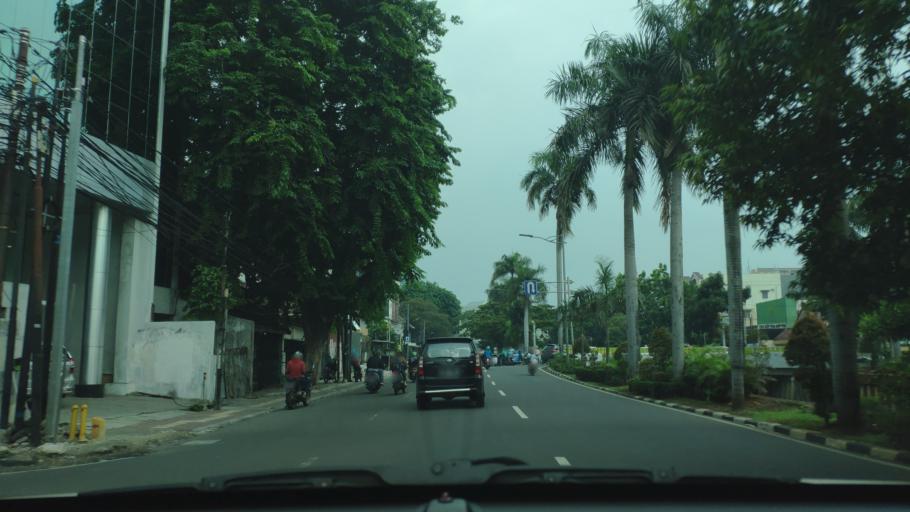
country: ID
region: Jakarta Raya
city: Jakarta
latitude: -6.1778
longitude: 106.8127
